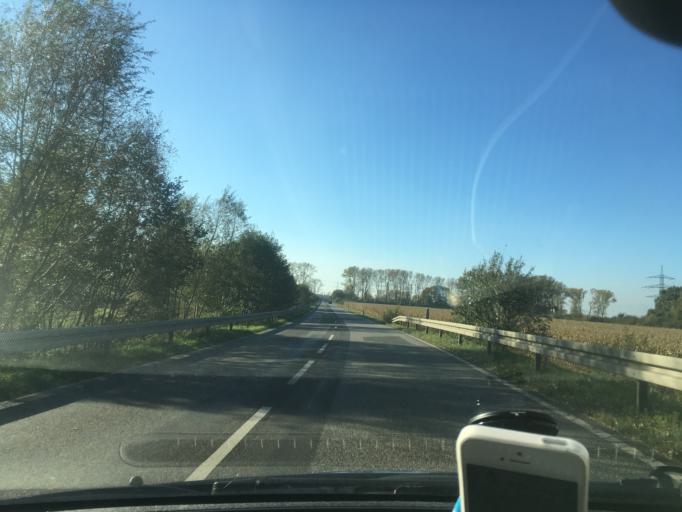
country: DE
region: Mecklenburg-Vorpommern
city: Wittenburg
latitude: 53.5194
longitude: 11.0814
